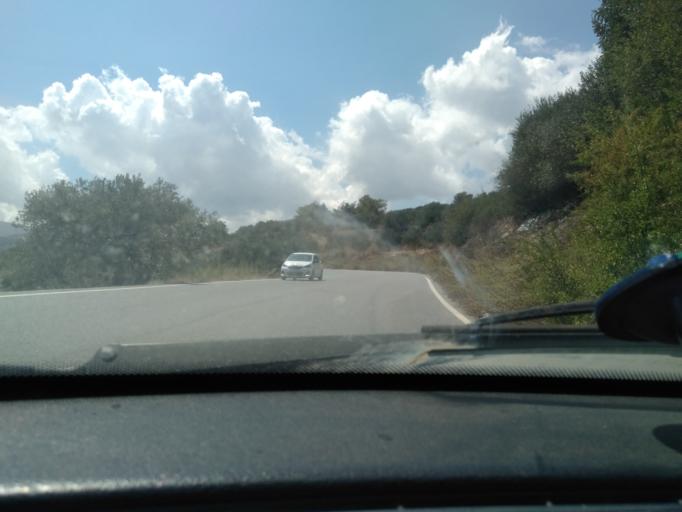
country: GR
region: Crete
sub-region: Nomos Lasithiou
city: Siteia
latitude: 35.1360
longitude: 26.0753
